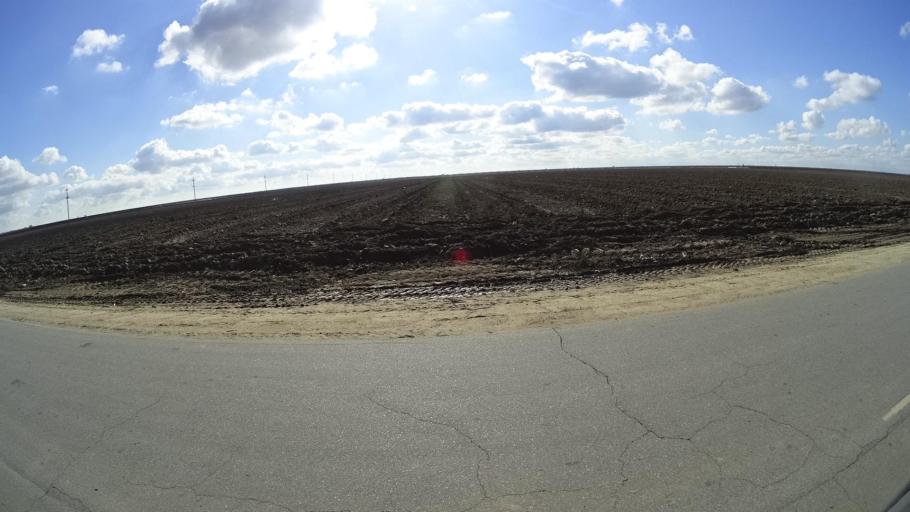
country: US
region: California
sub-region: Kern County
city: McFarland
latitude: 35.6743
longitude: -119.2781
